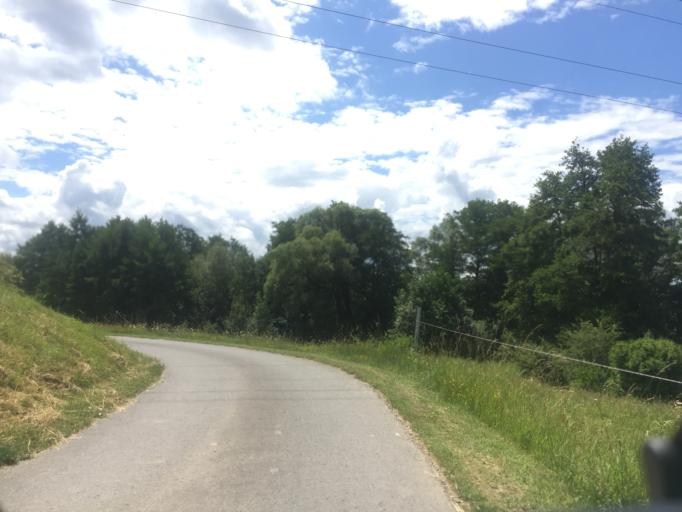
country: DE
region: Rheinland-Pfalz
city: Girod
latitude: 50.4557
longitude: 7.9263
